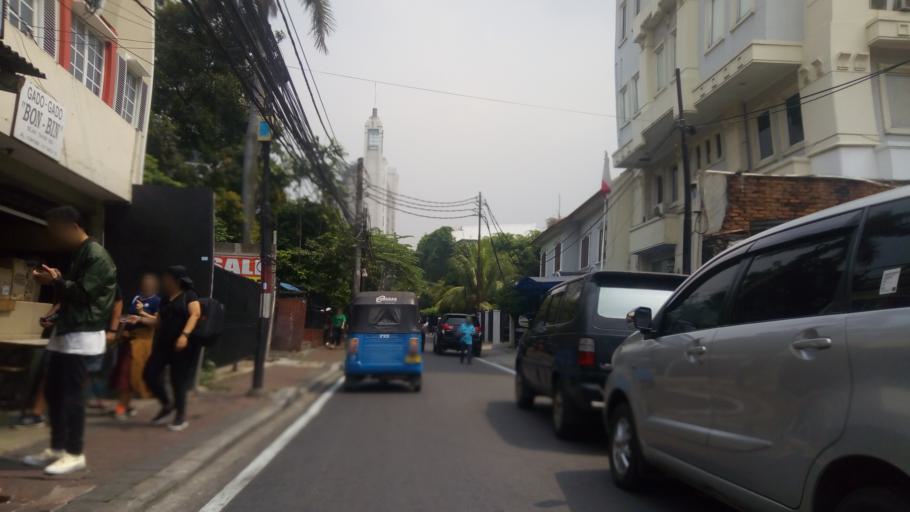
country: ID
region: Jakarta Raya
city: Jakarta
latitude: -6.1928
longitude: 106.8385
